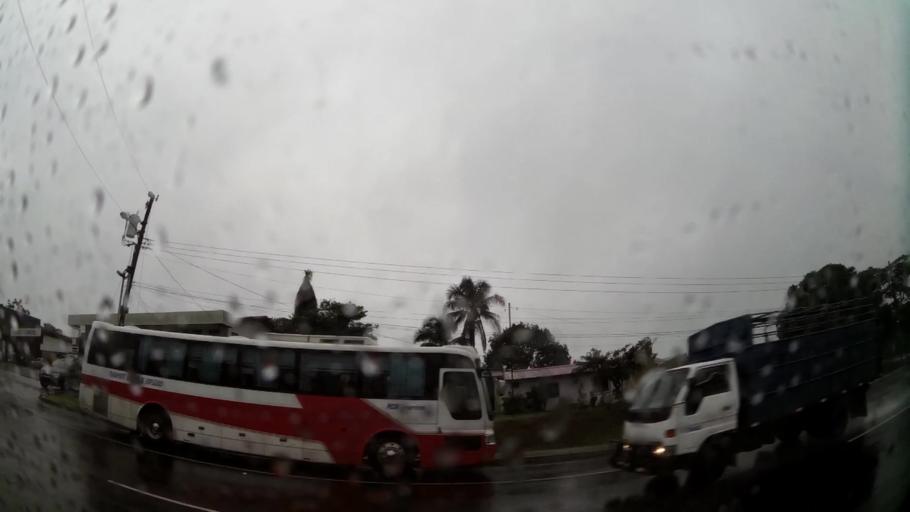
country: PA
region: Colon
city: Santa Rita Arriba
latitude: 9.3175
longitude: -79.7949
